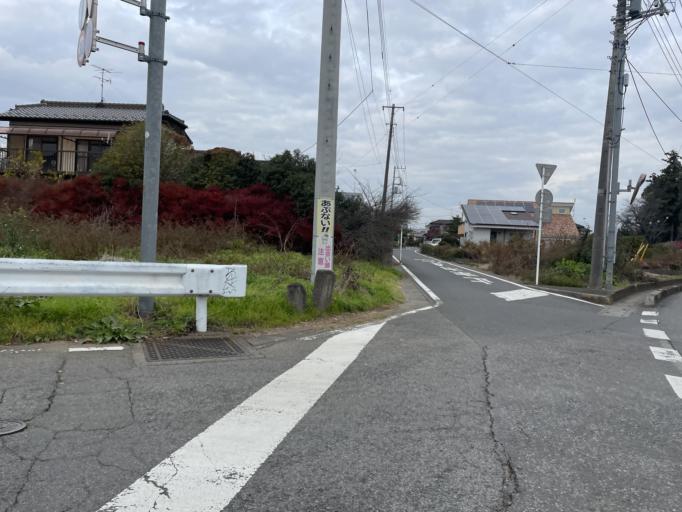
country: JP
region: Saitama
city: Shiraoka
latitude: 36.0057
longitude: 139.6613
